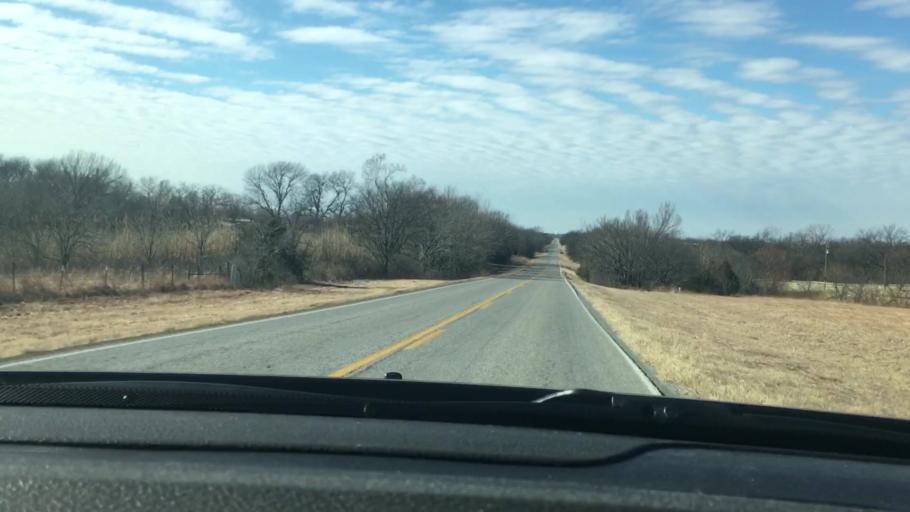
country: US
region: Oklahoma
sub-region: Garvin County
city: Wynnewood
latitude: 34.6515
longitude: -97.1113
